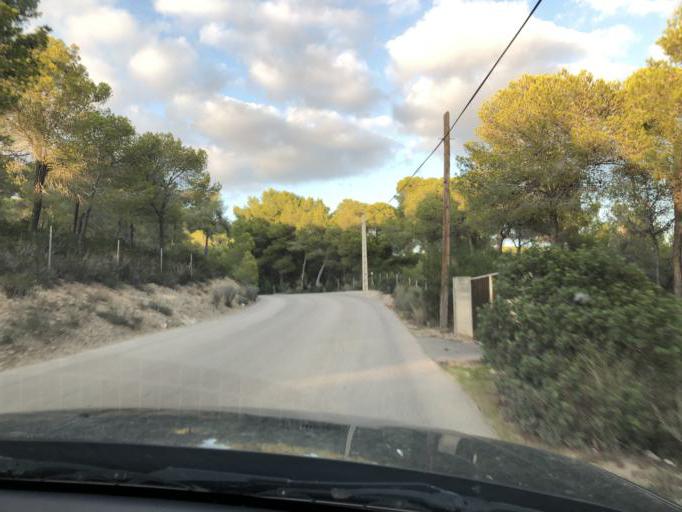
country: ES
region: Balearic Islands
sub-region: Illes Balears
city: Santa Ponsa
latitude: 39.5340
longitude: 2.4802
